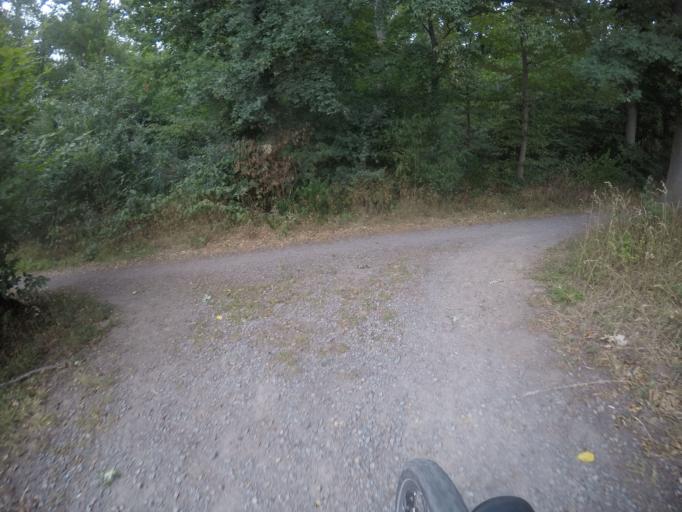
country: DE
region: Baden-Wuerttemberg
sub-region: Karlsruhe Region
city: Muhlacker
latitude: 48.9516
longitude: 8.8662
